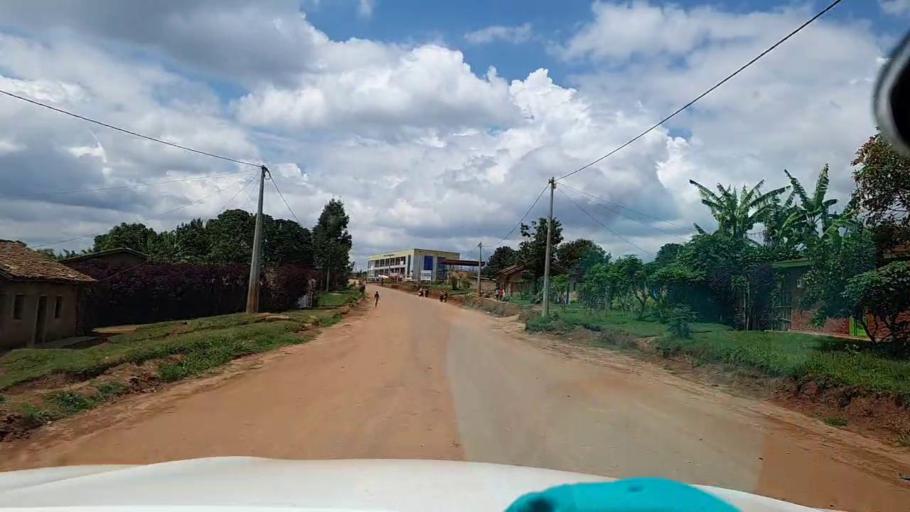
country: RW
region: Southern Province
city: Nzega
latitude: -2.6476
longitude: 29.5626
